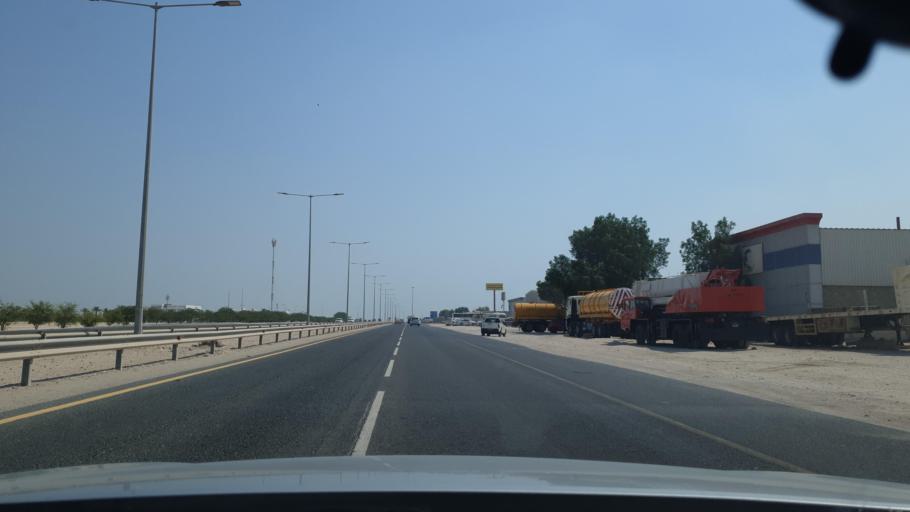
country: QA
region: Al Khawr
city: Al Khawr
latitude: 25.7174
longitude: 51.5041
